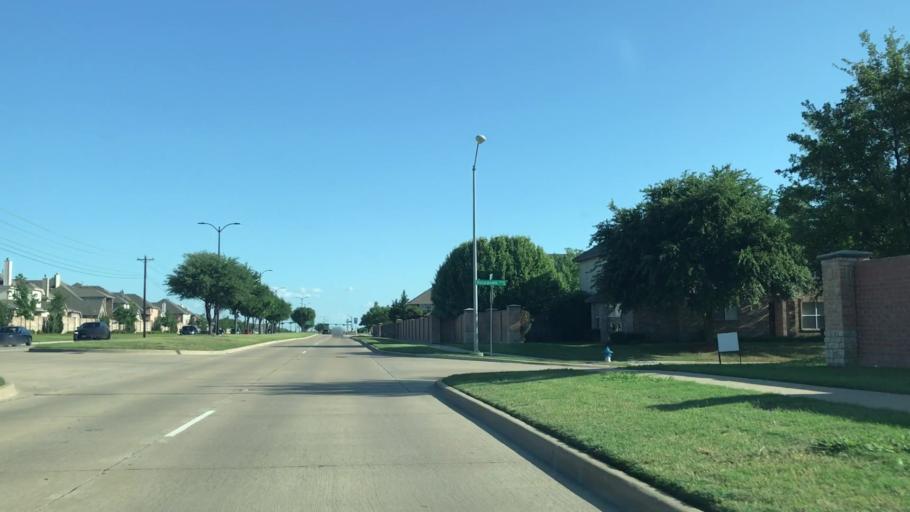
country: US
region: Texas
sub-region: Collin County
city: Frisco
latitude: 33.1340
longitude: -96.7681
